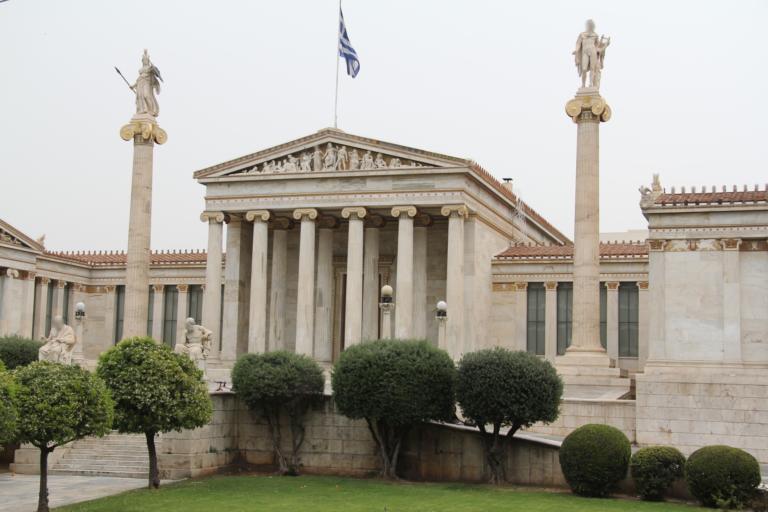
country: GR
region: Attica
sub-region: Nomarchia Athinas
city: Athens
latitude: 37.9801
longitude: 23.7341
